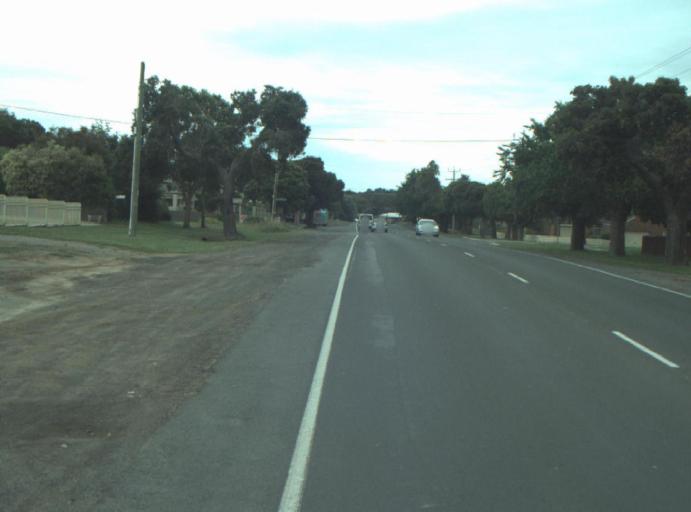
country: AU
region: Victoria
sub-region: Greater Geelong
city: Clifton Springs
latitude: -38.1755
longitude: 144.5678
